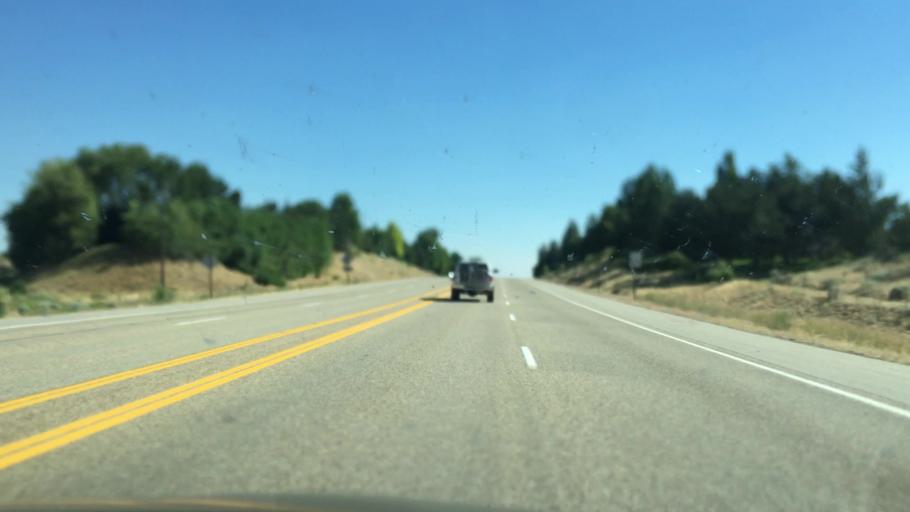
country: US
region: Idaho
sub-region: Ada County
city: Eagle
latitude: 43.7181
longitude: -116.3197
